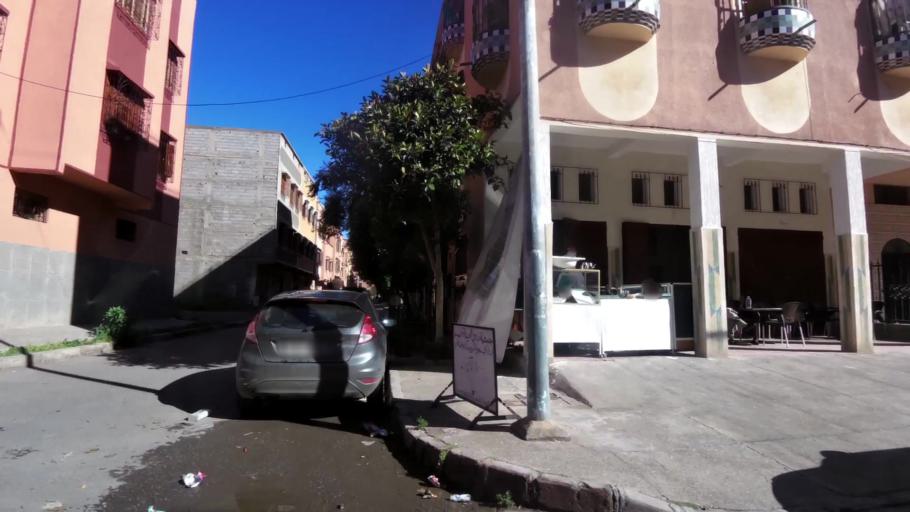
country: MA
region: Marrakech-Tensift-Al Haouz
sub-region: Marrakech
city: Marrakesh
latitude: 31.5998
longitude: -8.0419
